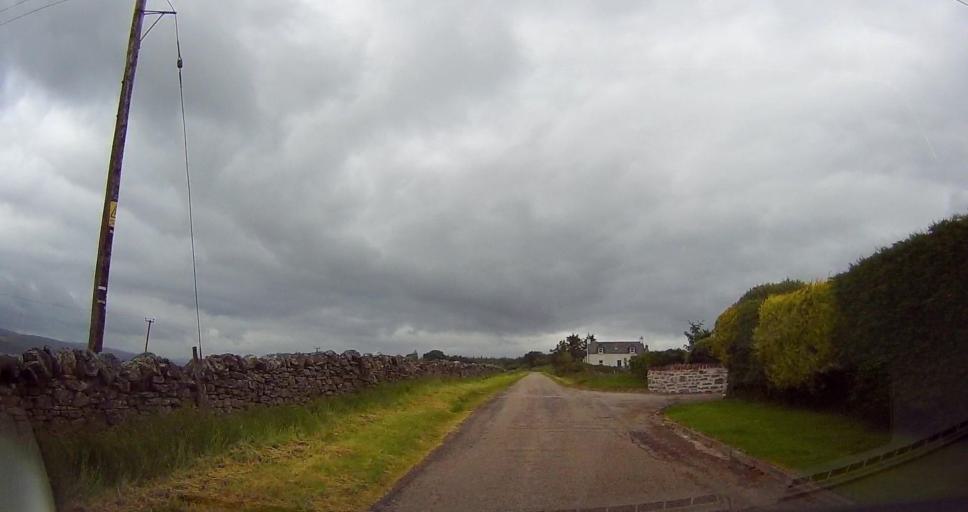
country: GB
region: Scotland
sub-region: Highland
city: Alness
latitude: 58.0781
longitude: -4.4448
